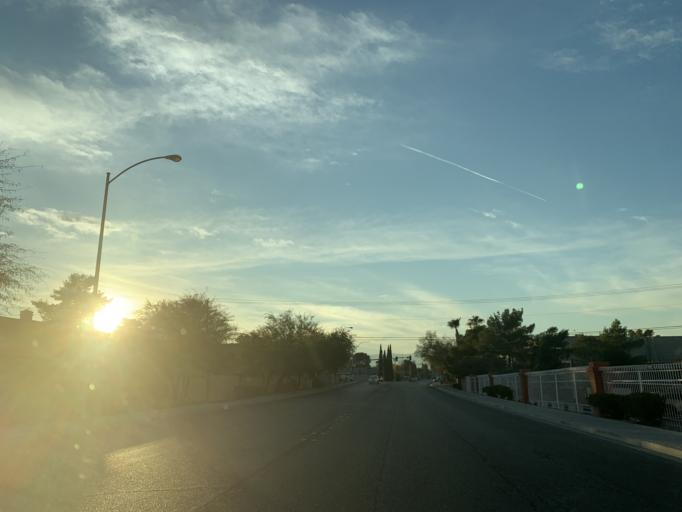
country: US
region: Nevada
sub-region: Clark County
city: Spring Valley
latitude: 36.0964
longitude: -115.2231
